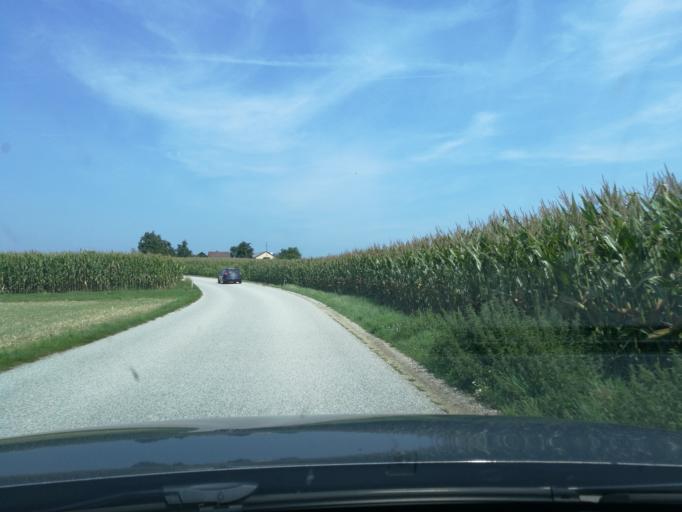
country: AT
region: Upper Austria
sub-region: Politischer Bezirk Grieskirchen
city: Grieskirchen
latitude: 48.2946
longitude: 13.7996
